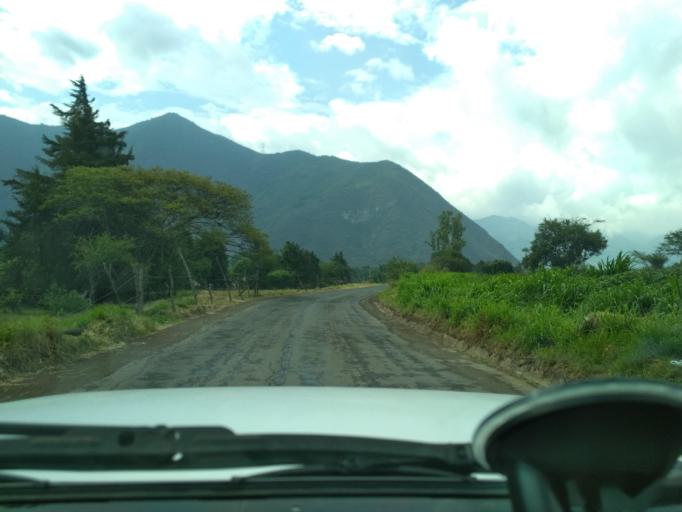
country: MX
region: Veracruz
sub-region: Nogales
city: Taza de Agua Ojo Zarco
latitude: 18.7824
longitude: -97.2005
